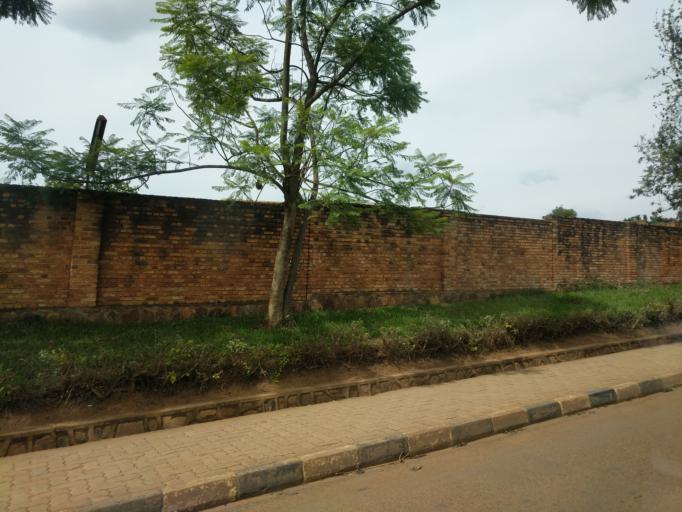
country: RW
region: Kigali
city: Kigali
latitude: -1.9703
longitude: 30.1279
